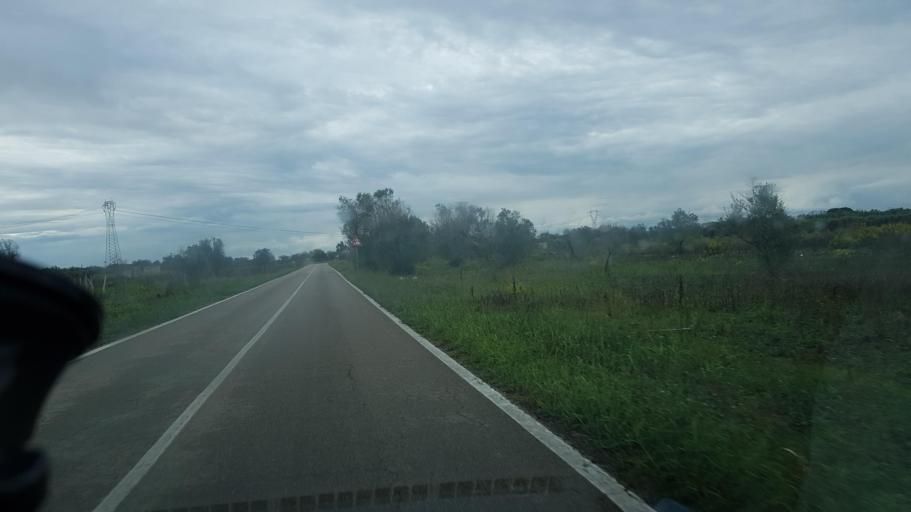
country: IT
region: Apulia
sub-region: Provincia di Lecce
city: Campi Salentina
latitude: 40.3661
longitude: 17.9991
